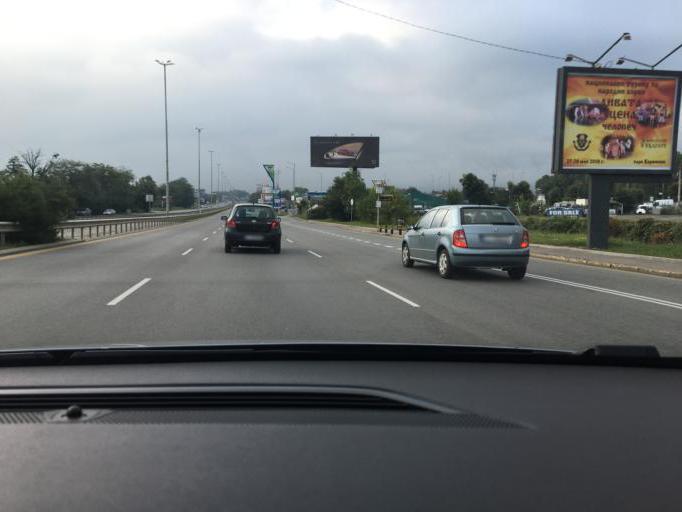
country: BG
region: Sofia-Capital
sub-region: Stolichna Obshtina
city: Sofia
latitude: 42.6428
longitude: 23.4026
